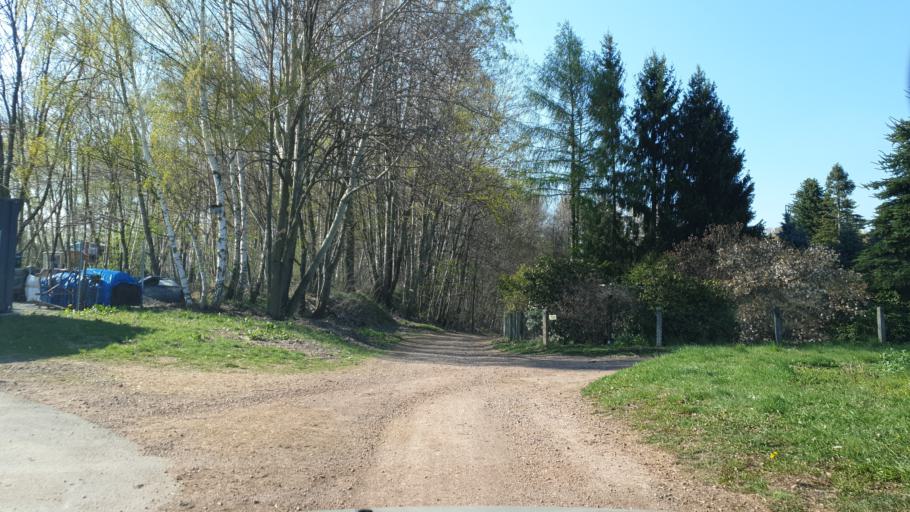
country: DE
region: Saxony
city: Oelsnitz
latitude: 50.7368
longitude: 12.6919
